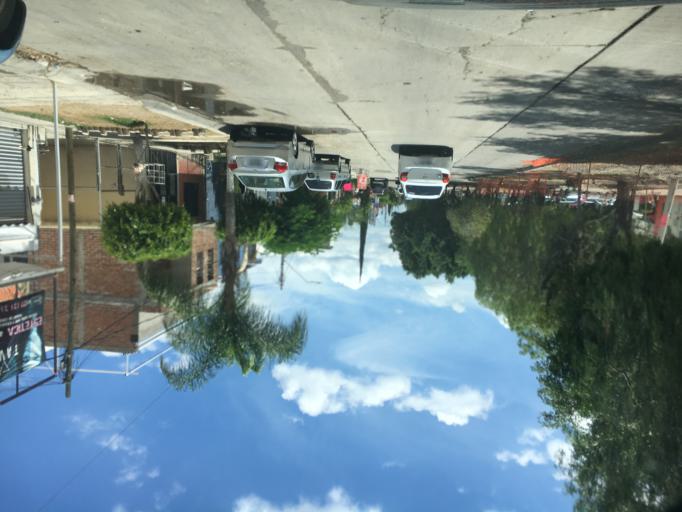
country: MX
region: Guanajuato
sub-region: Leon
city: San Jose de Duran (Los Troncoso)
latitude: 21.0761
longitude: -101.6450
